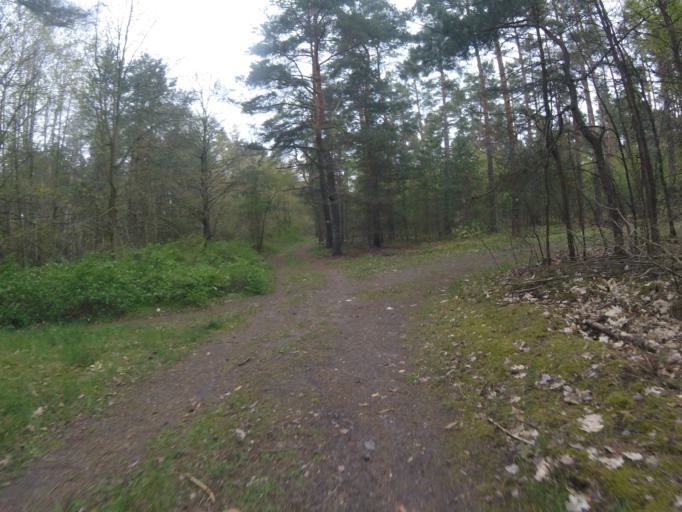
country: DE
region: Brandenburg
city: Bestensee
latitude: 52.2445
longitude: 13.6659
